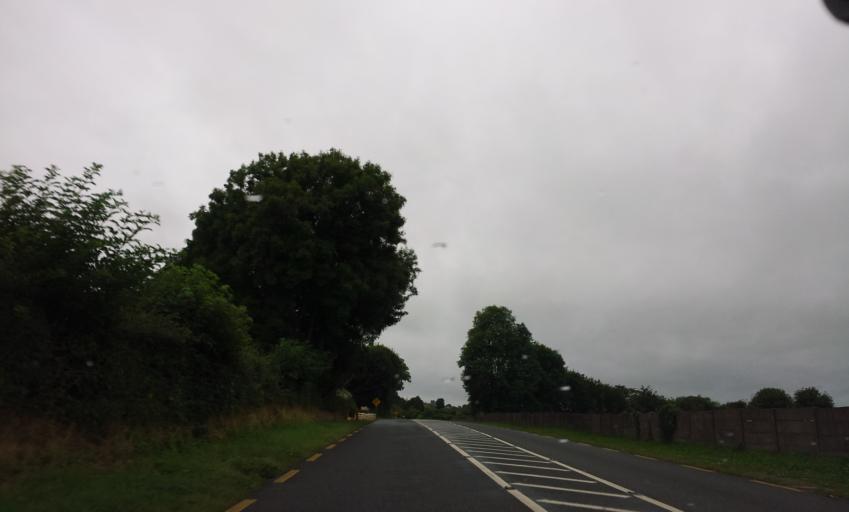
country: IE
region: Munster
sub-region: County Cork
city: Mitchelstown
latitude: 52.2481
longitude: -8.4097
